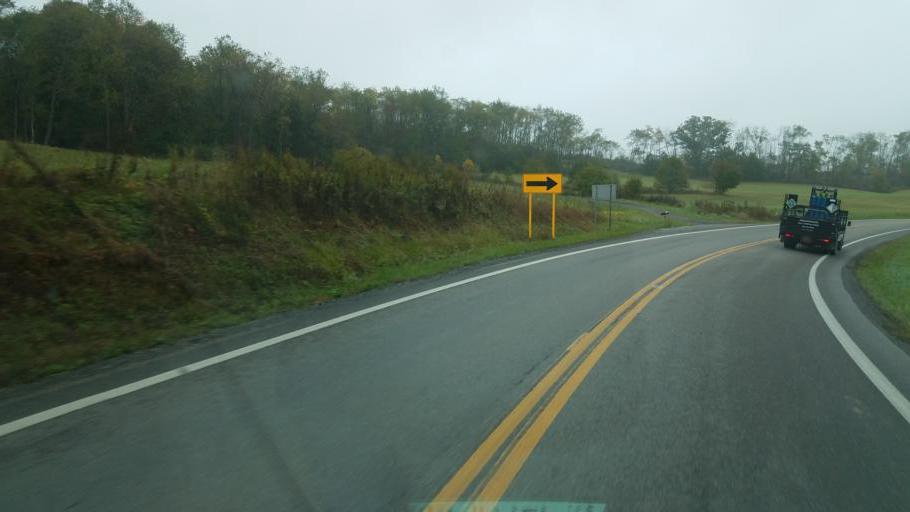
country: US
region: Ohio
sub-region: Tuscarawas County
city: Rockford
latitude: 40.4251
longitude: -81.1582
